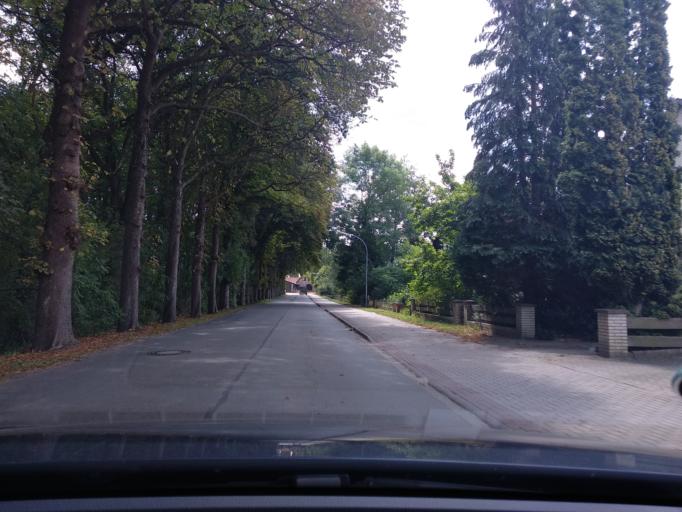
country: DE
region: Lower Saxony
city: Wagenhoff
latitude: 52.5106
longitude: 10.4817
